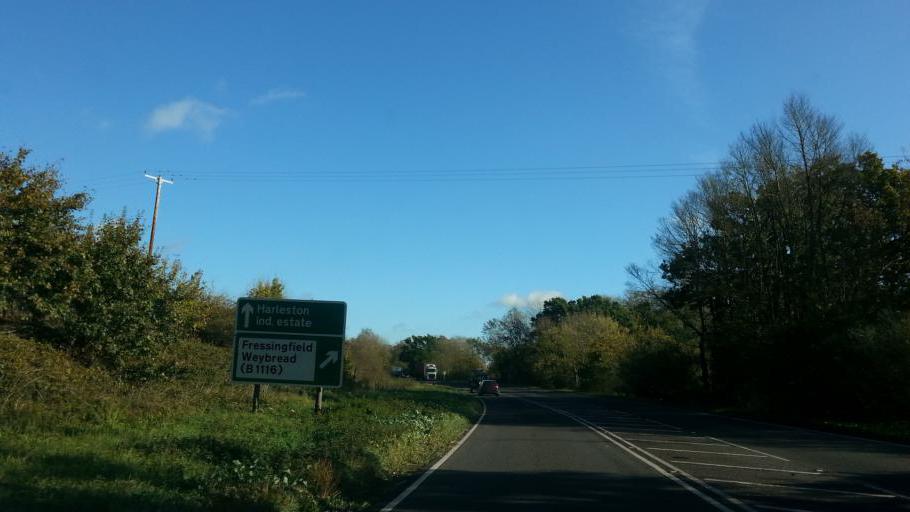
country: GB
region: England
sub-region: Norfolk
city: Harleston
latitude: 52.3918
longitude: 1.2870
